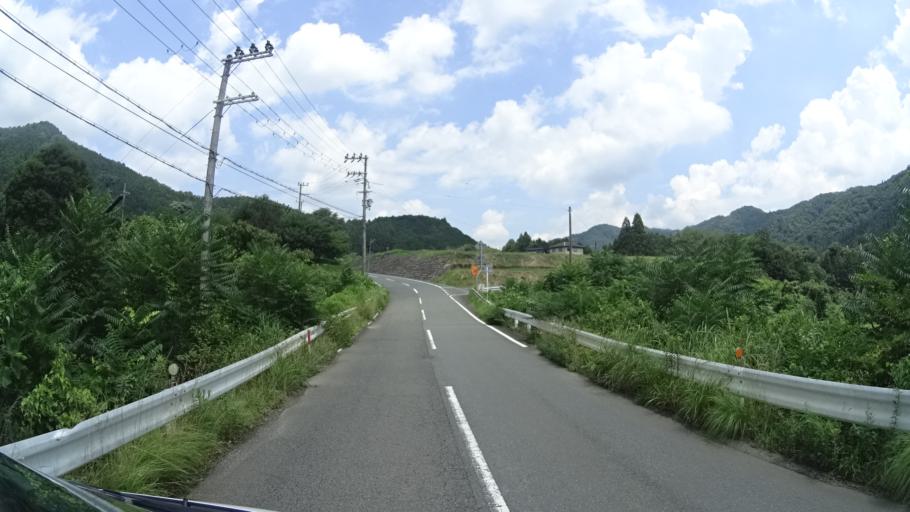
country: JP
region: Kyoto
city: Ayabe
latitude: 35.2025
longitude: 135.2438
